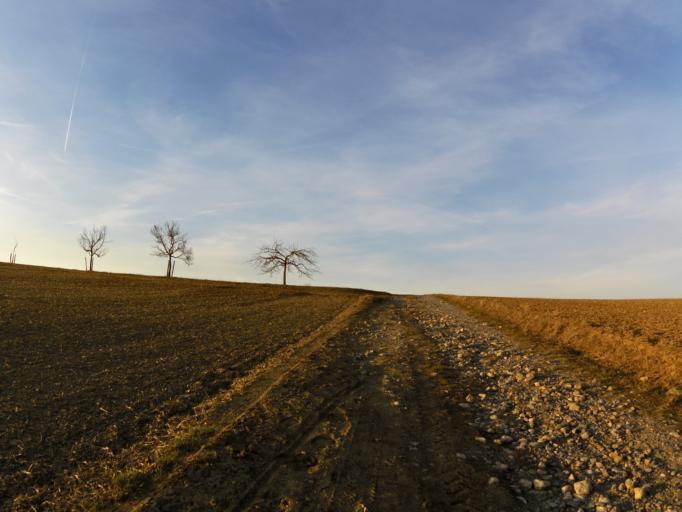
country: DE
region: Bavaria
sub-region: Regierungsbezirk Unterfranken
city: Estenfeld
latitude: 49.8223
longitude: 10.0219
